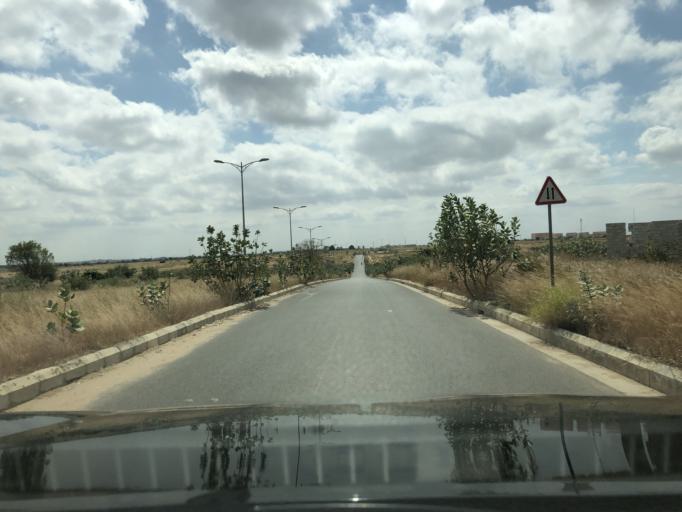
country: AO
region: Luanda
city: Luanda
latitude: -8.9671
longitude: 13.2419
